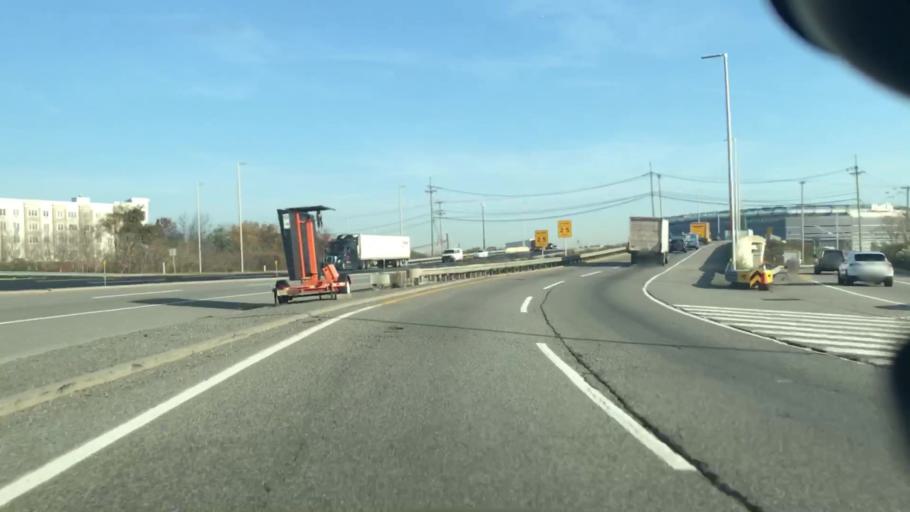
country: US
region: New Jersey
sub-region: Hudson County
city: Secaucus
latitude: 40.8060
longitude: -74.0812
